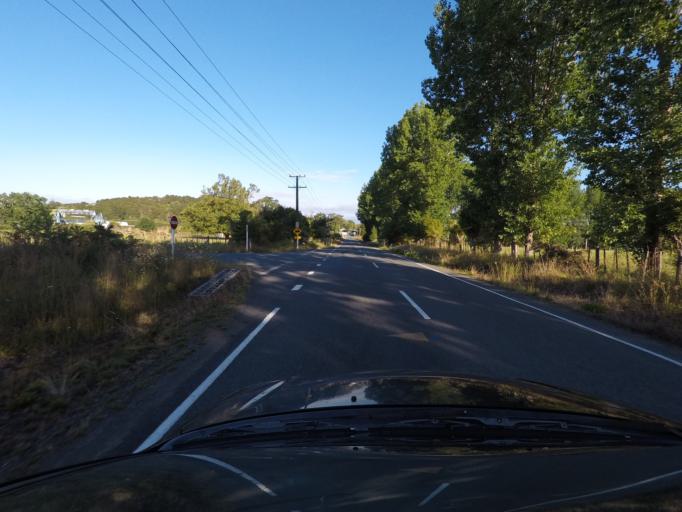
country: NZ
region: Northland
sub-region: Whangarei
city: Whangarei
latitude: -35.6436
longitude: 174.3005
